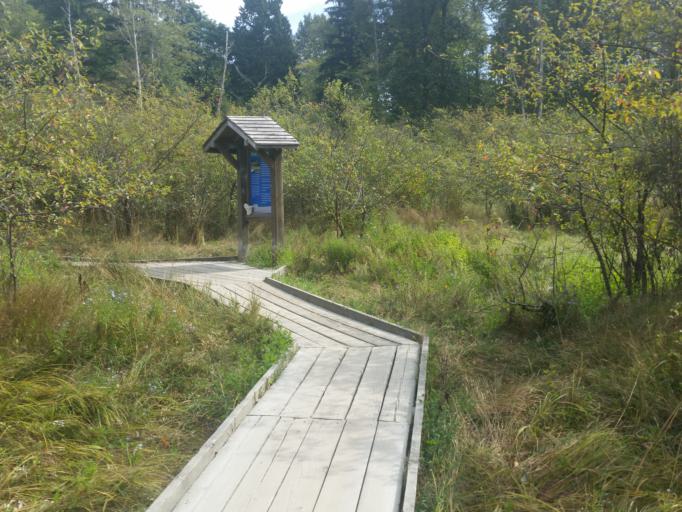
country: CA
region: British Columbia
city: Port Moody
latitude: 49.2810
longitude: -122.8351
